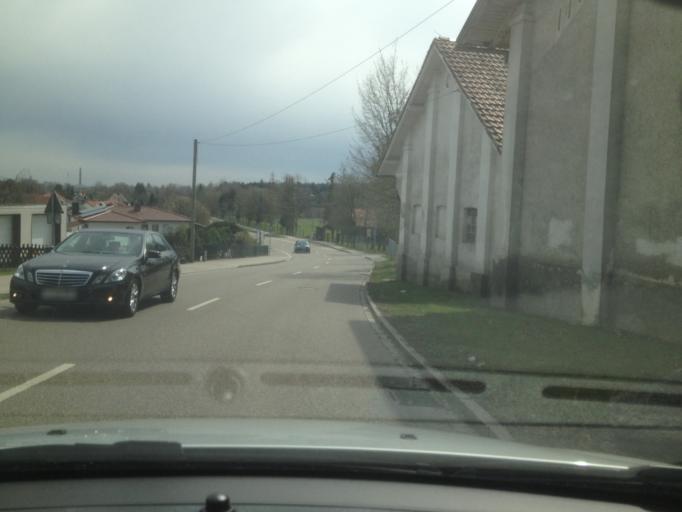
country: DE
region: Bavaria
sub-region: Swabia
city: Wehringen
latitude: 48.2724
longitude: 10.7898
